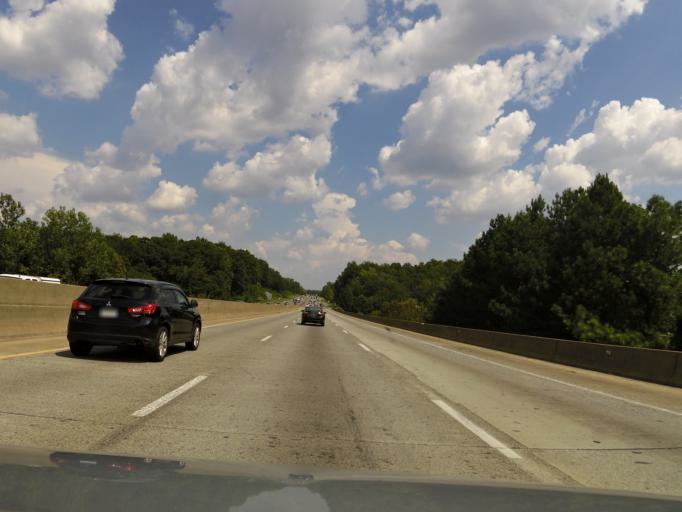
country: US
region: North Carolina
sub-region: Gaston County
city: Lowell
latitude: 35.2642
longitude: -81.0796
